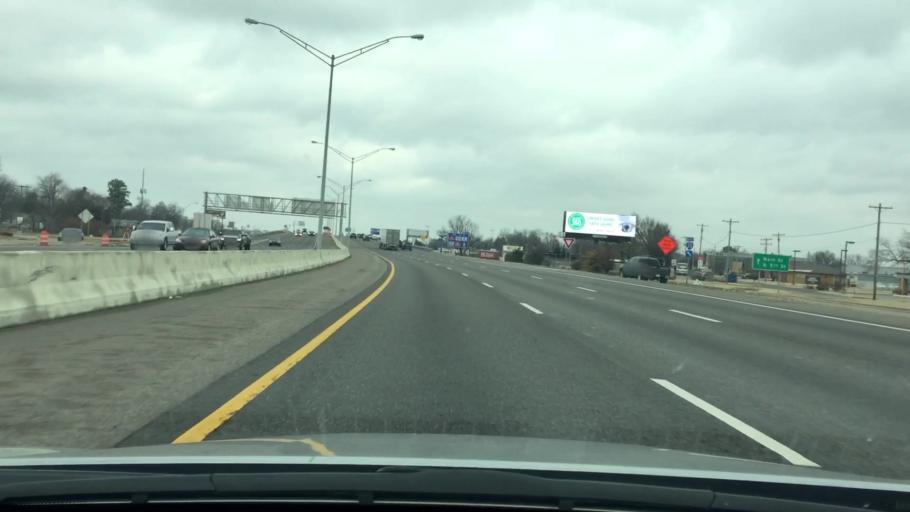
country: US
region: Oklahoma
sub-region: Cleveland County
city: Moore
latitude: 35.3349
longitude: -97.4903
